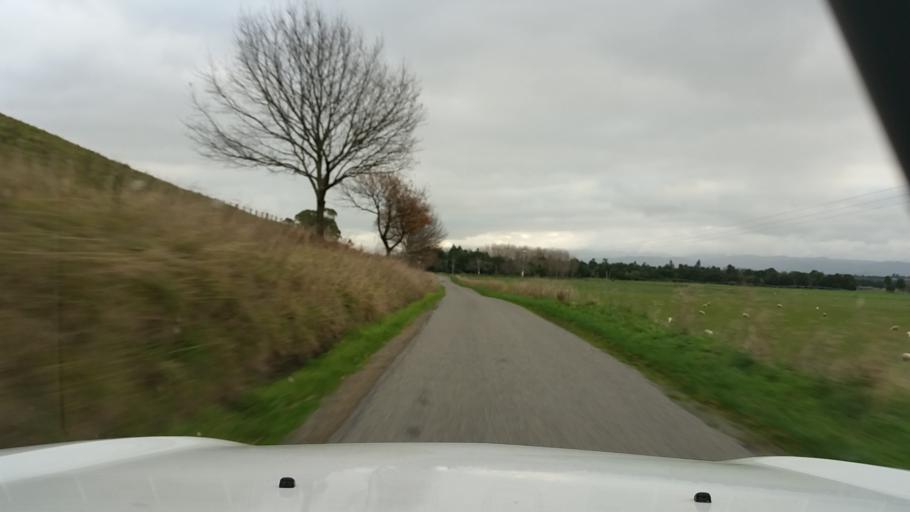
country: NZ
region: Wellington
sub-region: Masterton District
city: Masterton
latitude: -41.0493
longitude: 175.6844
